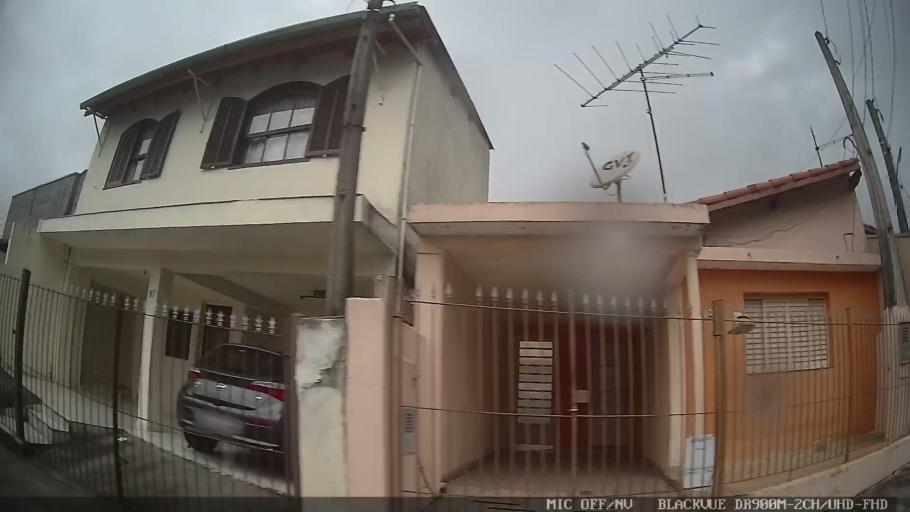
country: BR
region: Sao Paulo
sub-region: Mogi das Cruzes
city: Mogi das Cruzes
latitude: -23.5188
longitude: -46.1760
